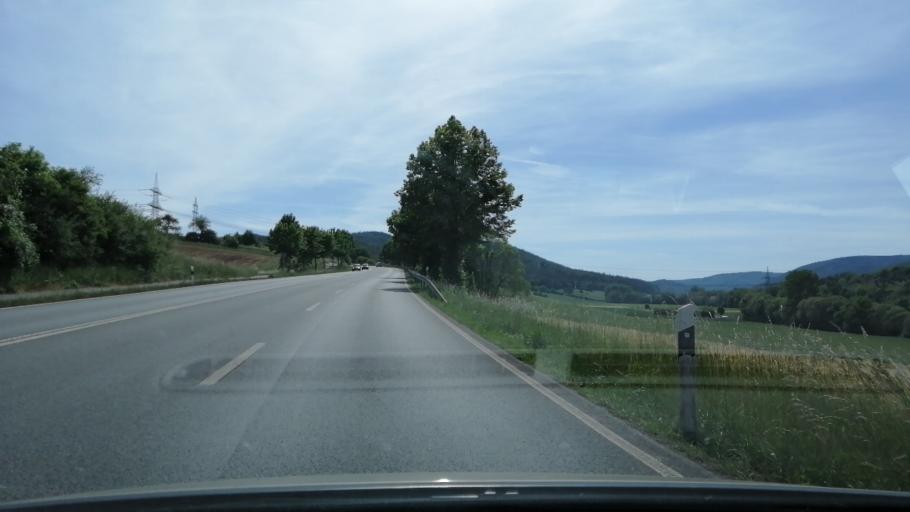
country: DE
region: Hesse
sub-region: Regierungsbezirk Kassel
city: Bad Wildungen
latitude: 51.1515
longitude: 9.1208
